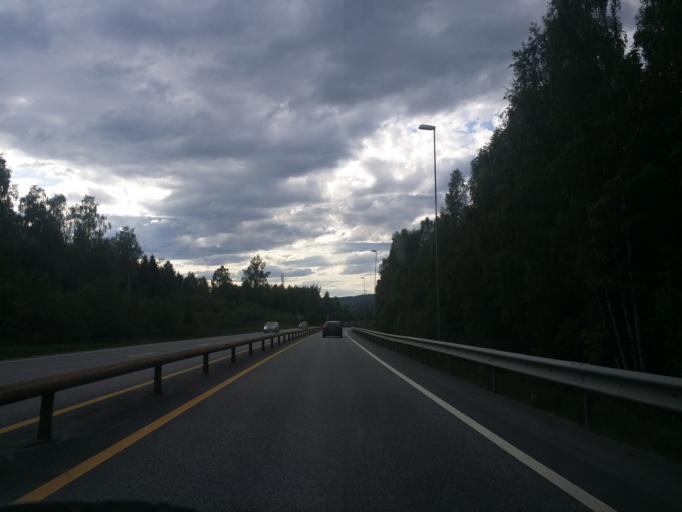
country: NO
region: Hedmark
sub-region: Hamar
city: Hamar
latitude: 60.7815
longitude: 11.1383
